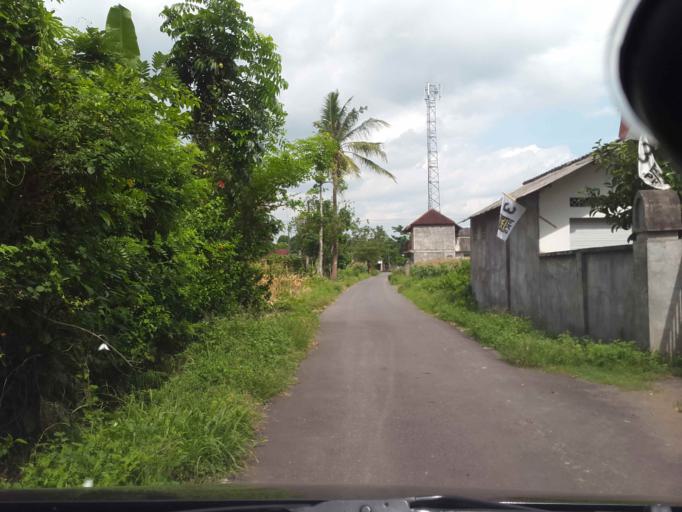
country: ID
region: West Nusa Tenggara
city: Karangkebon Timur
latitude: -8.6548
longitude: 116.1306
